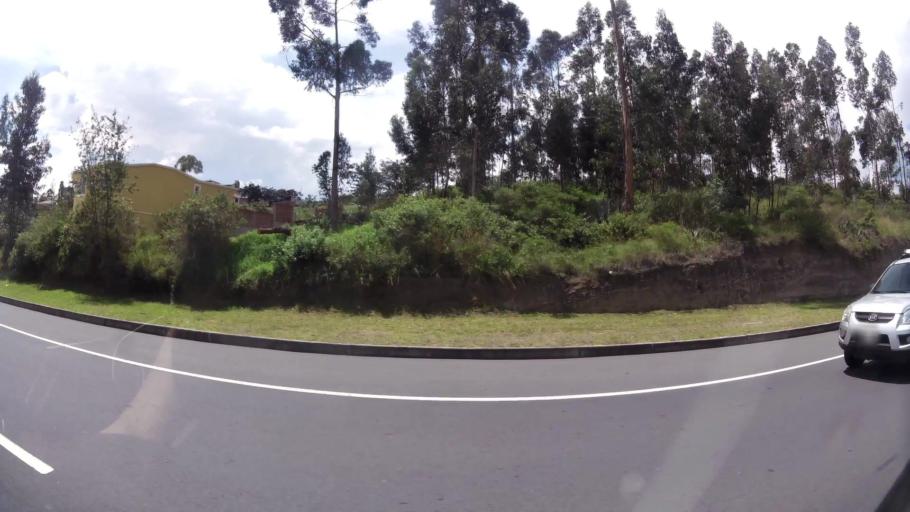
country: EC
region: Pichincha
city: Sangolqui
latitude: -0.1806
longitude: -78.3410
